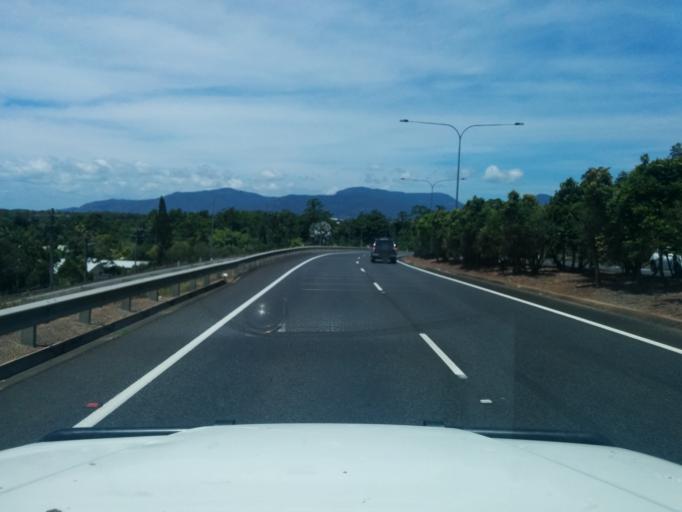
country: AU
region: Queensland
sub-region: Cairns
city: Cairns
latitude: -16.9145
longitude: 145.7281
